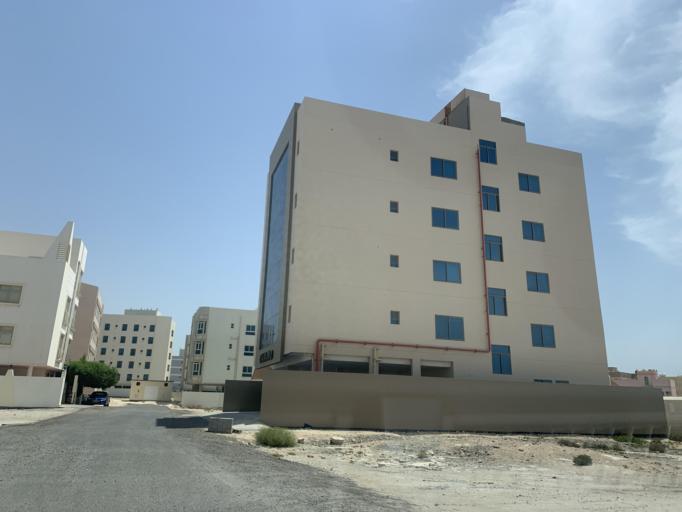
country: BH
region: Northern
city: Madinat `Isa
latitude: 26.1865
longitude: 50.4796
